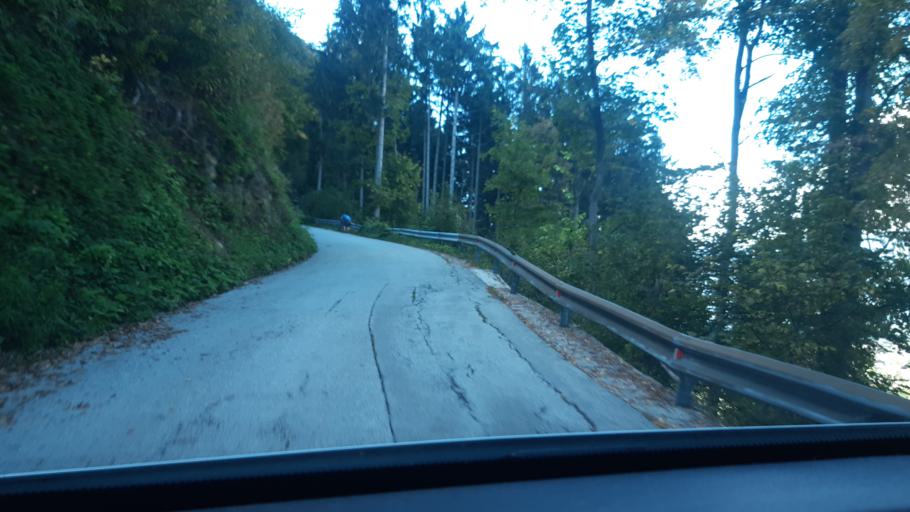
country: SI
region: Kranj
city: Kranj
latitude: 46.2401
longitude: 14.3450
